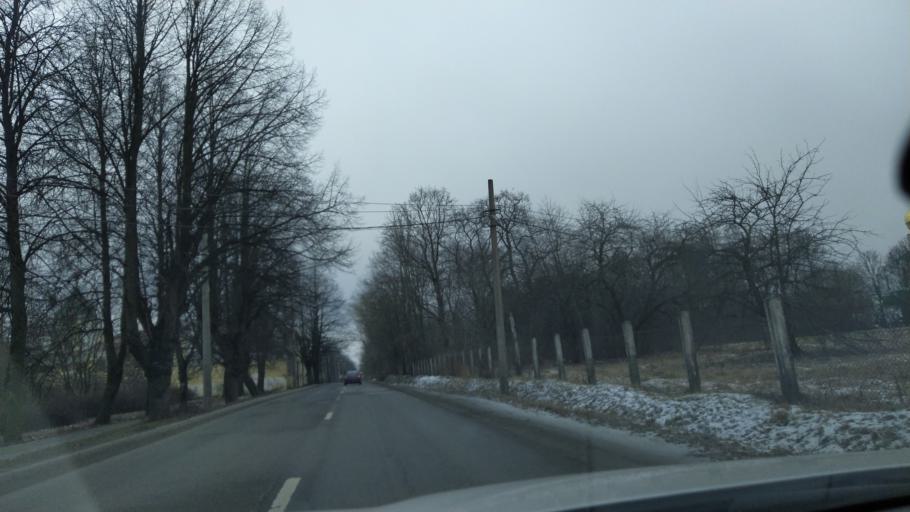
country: RU
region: St.-Petersburg
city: Pushkin
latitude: 59.7278
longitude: 30.3897
